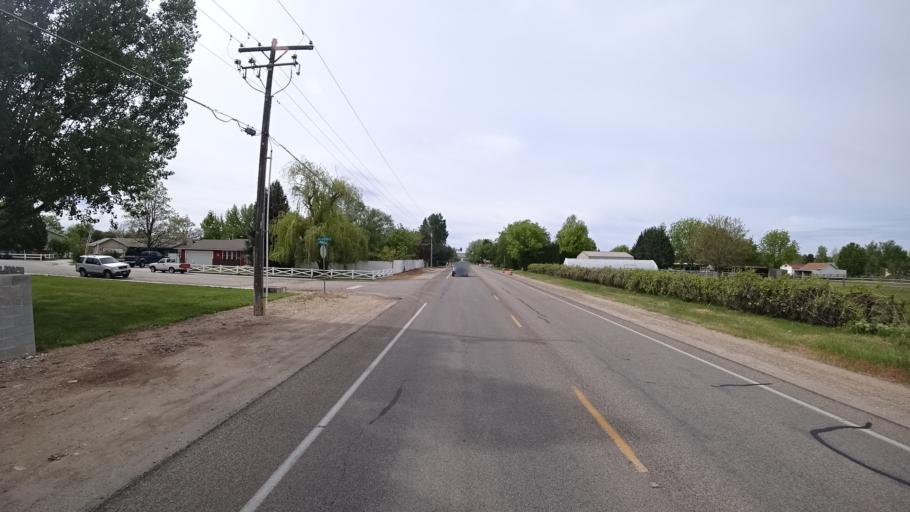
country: US
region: Idaho
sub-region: Ada County
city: Garden City
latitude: 43.5551
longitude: -116.2942
